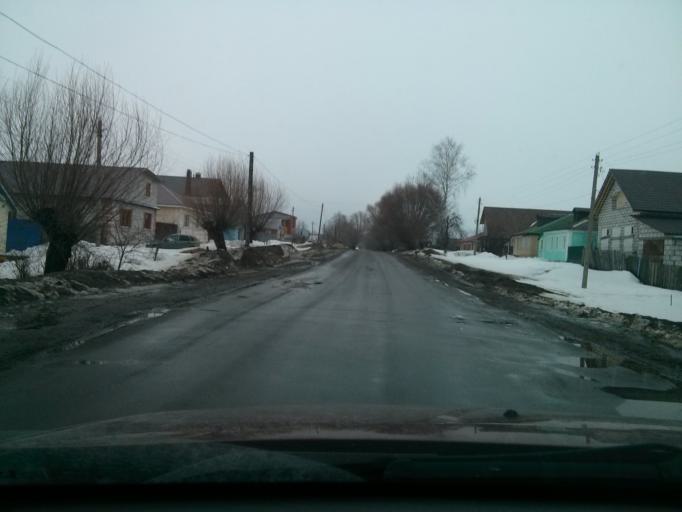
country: RU
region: Vladimir
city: Murom
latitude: 55.5370
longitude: 42.0246
